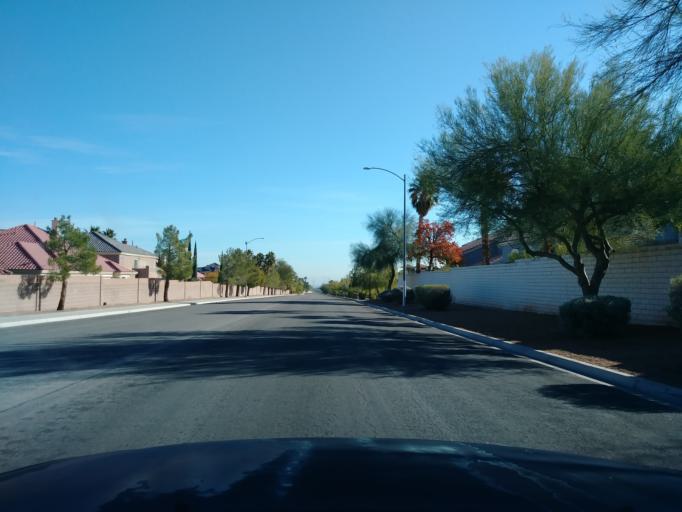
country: US
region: Nevada
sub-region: Clark County
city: Spring Valley
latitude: 36.1459
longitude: -115.2753
